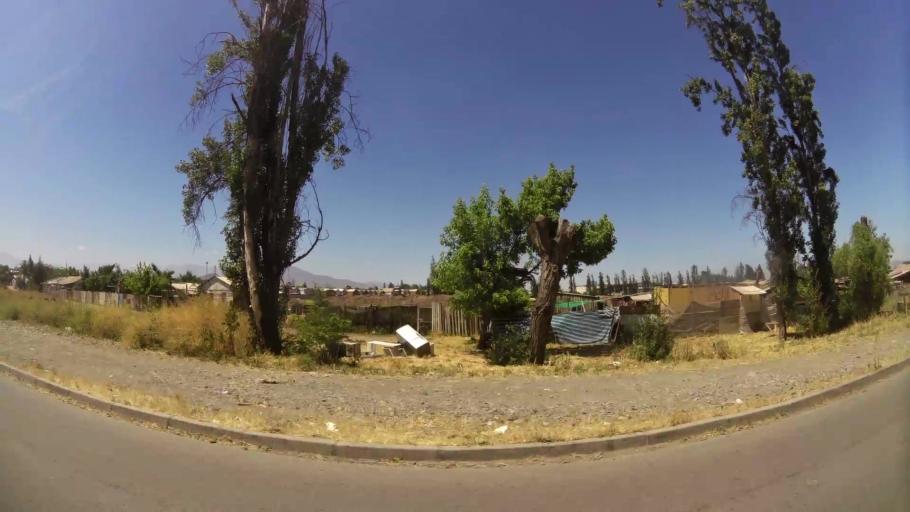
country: CL
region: Santiago Metropolitan
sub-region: Provincia de Maipo
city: San Bernardo
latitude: -33.6253
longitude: -70.7095
